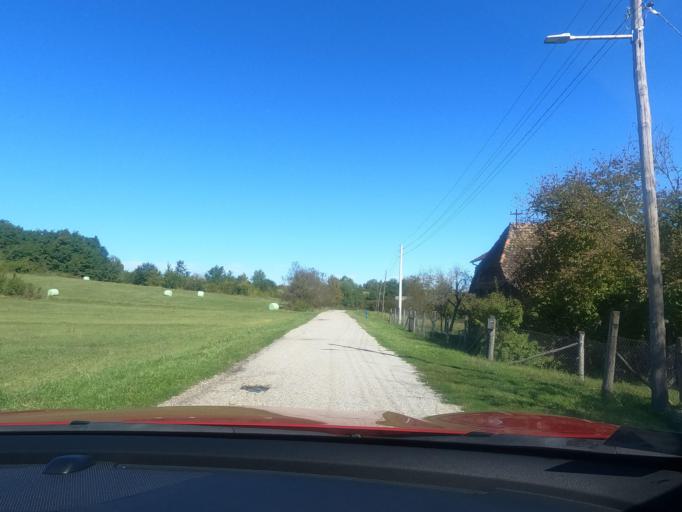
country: HR
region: Sisacko-Moslavacka
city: Petrinja
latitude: 45.3564
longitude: 16.2178
